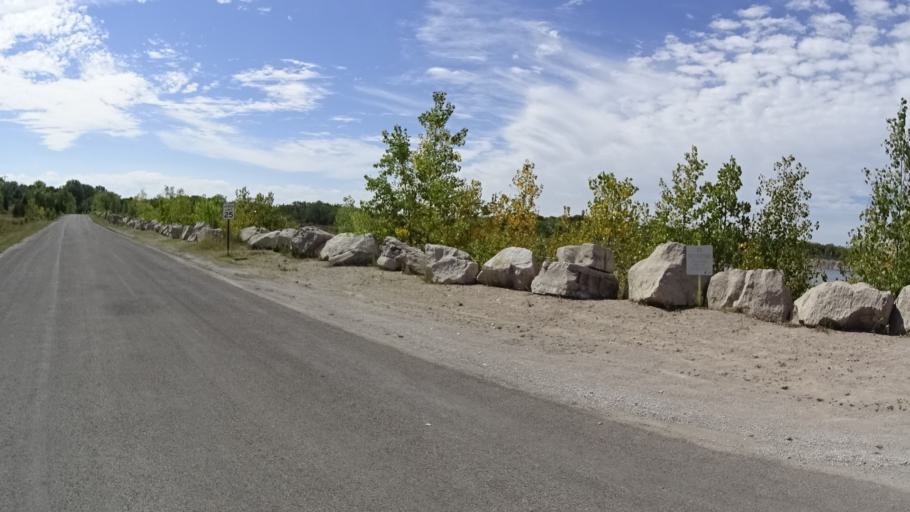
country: US
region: Ohio
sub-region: Erie County
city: Sandusky
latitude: 41.6040
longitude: -82.7209
